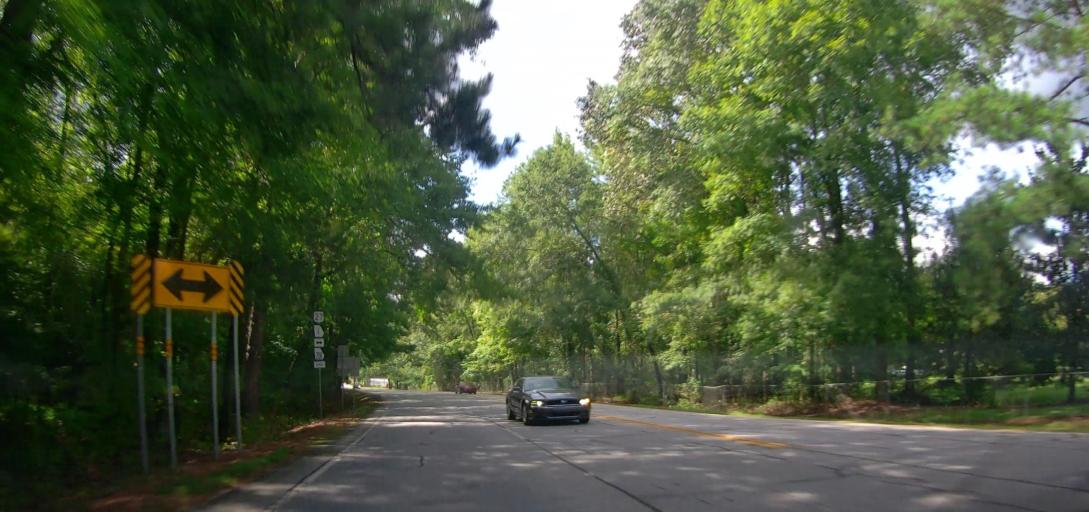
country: US
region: Georgia
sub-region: Harris County
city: Hamilton
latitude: 32.7024
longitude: -84.8599
